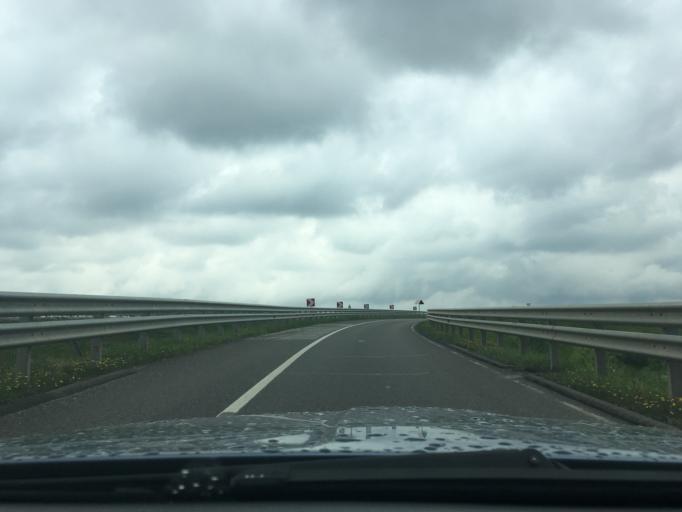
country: HU
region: Hajdu-Bihar
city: Debrecen
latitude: 47.5511
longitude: 21.5532
